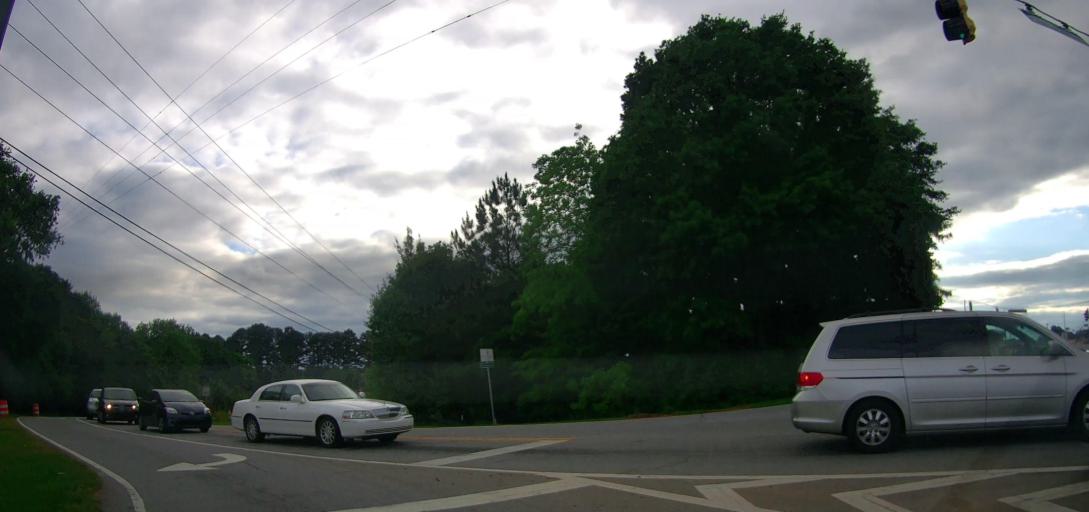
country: US
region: Georgia
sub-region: Clarke County
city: Country Club Estates
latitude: 33.9390
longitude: -83.4601
